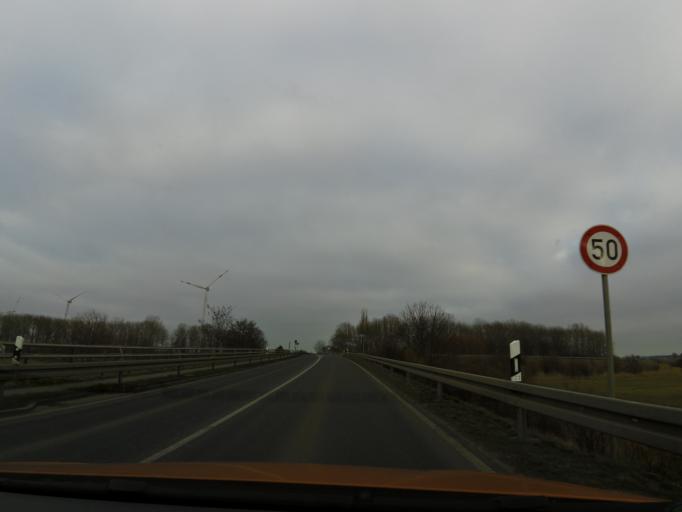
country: DE
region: Brandenburg
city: Dabergotz
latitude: 52.9055
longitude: 12.7350
